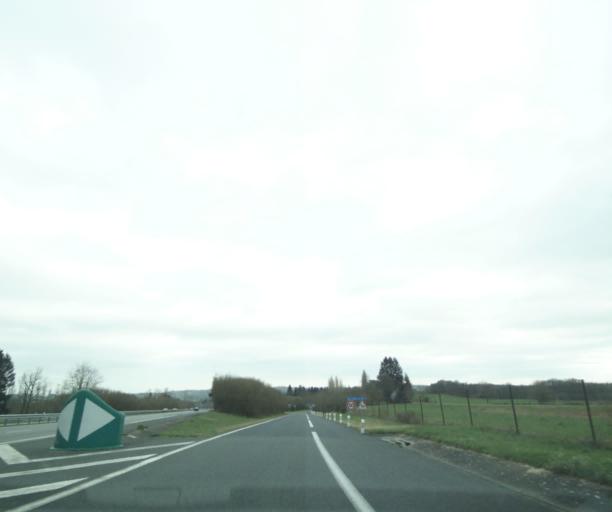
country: FR
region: Limousin
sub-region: Departement de la Correze
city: Vigeois
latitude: 45.3627
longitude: 1.5703
